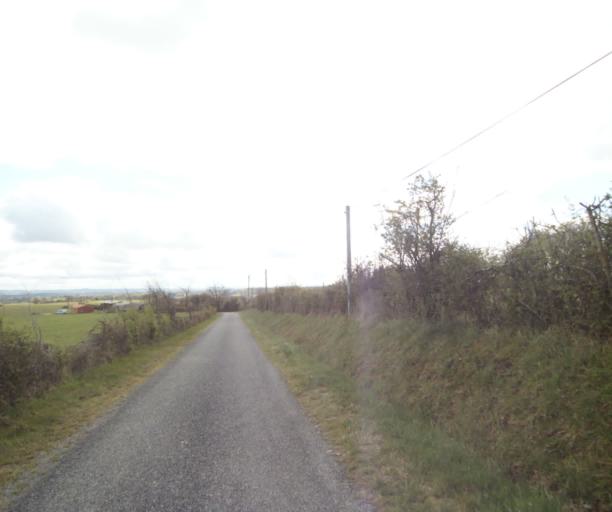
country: FR
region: Midi-Pyrenees
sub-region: Departement de l'Ariege
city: Saverdun
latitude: 43.2289
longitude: 1.5290
